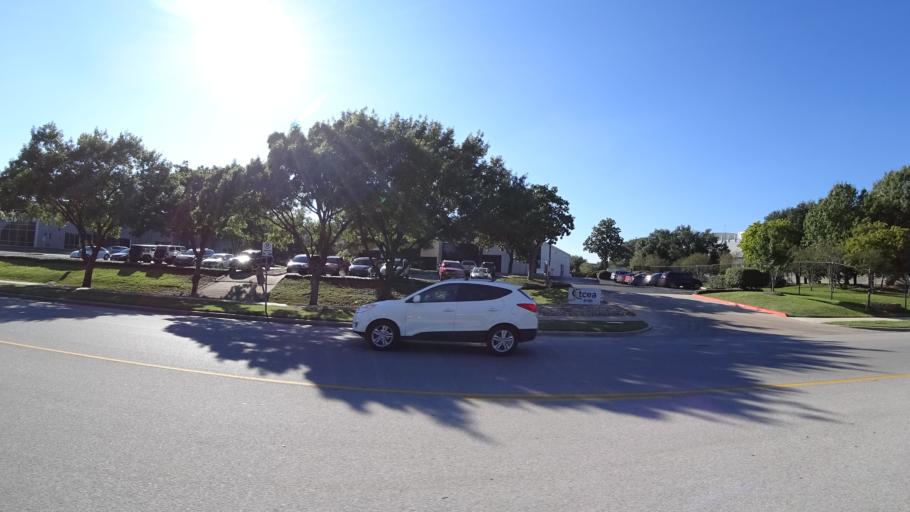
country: US
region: Texas
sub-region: Travis County
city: Austin
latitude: 30.2158
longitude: -97.7204
